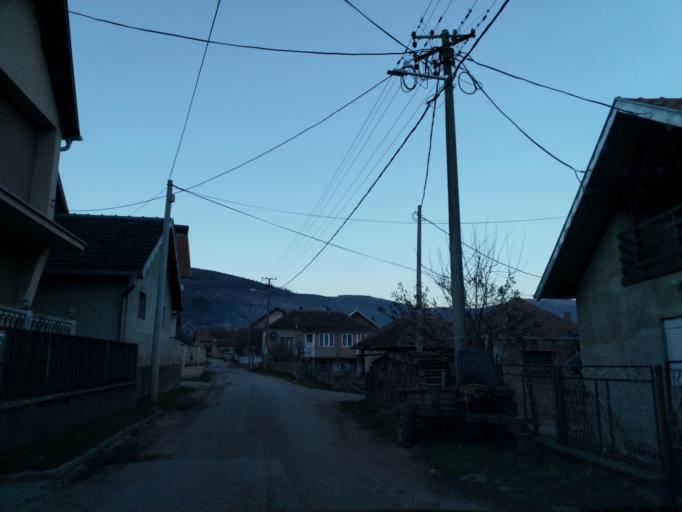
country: RS
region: Central Serbia
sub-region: Pomoravski Okrug
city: Paracin
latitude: 43.9308
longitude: 21.5193
